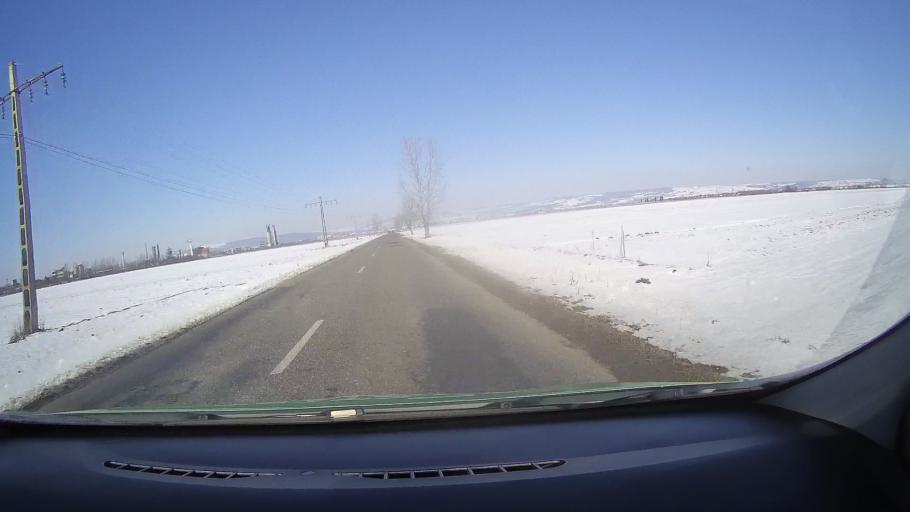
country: RO
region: Brasov
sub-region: Comuna Harseni
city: Harseni
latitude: 45.7993
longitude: 24.9934
